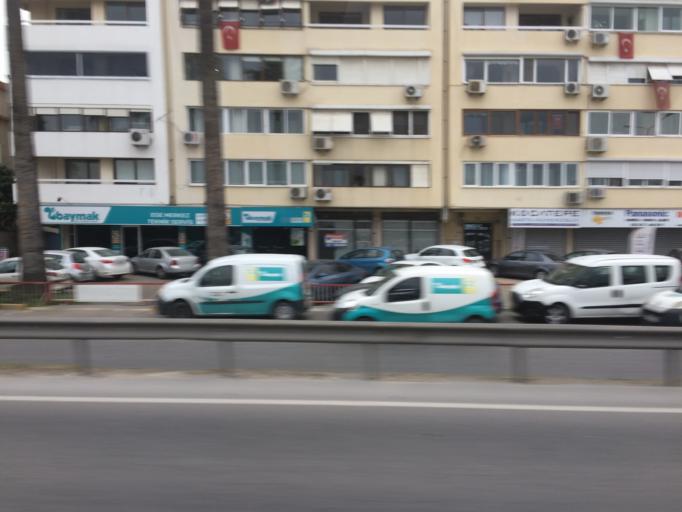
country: TR
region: Izmir
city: Karsiyaka
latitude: 38.4641
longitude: 27.1628
